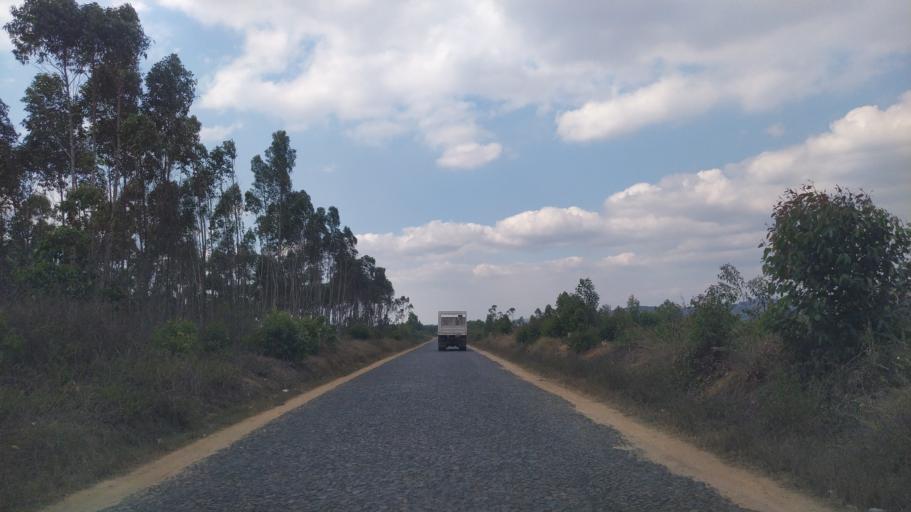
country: MG
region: Alaotra Mangoro
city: Moramanga
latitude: -18.7733
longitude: 48.2504
